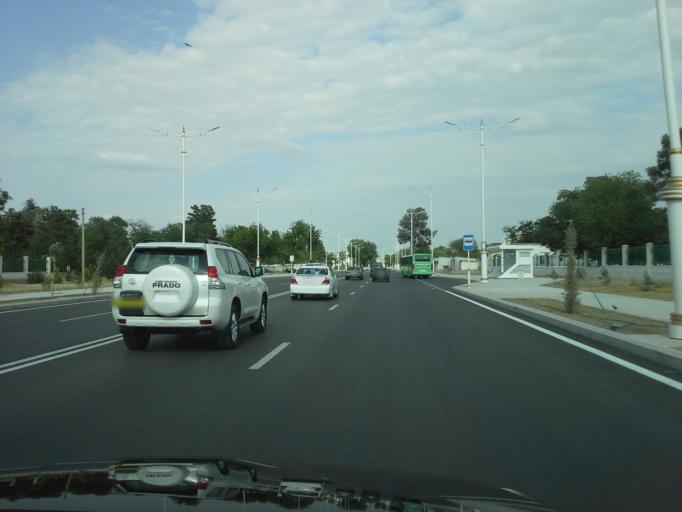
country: TM
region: Ahal
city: Ashgabat
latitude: 37.9583
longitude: 58.3407
